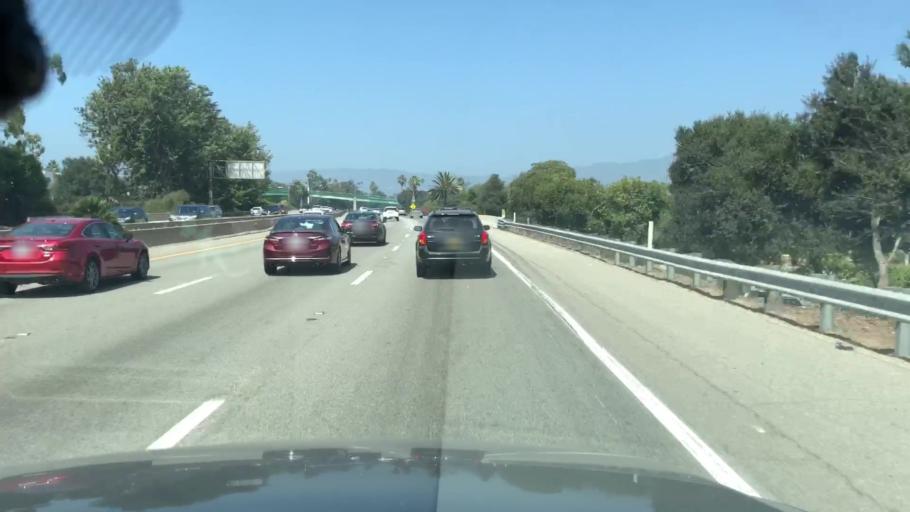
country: US
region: California
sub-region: Santa Barbara County
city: Santa Barbara
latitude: 34.4160
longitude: -119.7065
